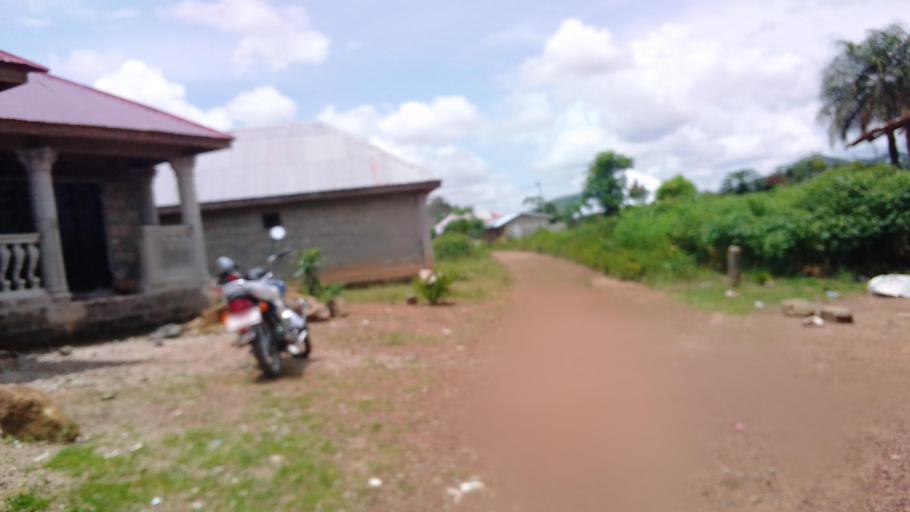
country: SL
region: Northern Province
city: Makeni
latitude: 8.8637
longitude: -12.0368
